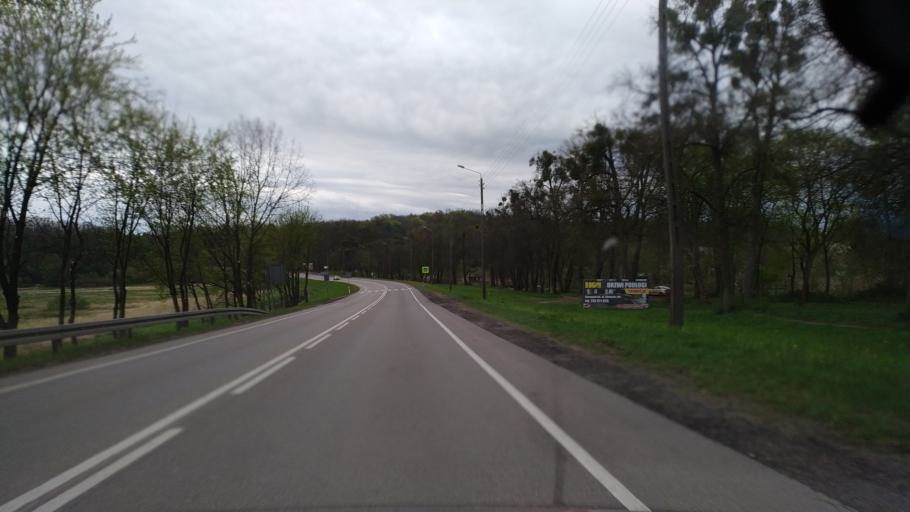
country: PL
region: Pomeranian Voivodeship
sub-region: Powiat starogardzki
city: Starogard Gdanski
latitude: 53.9717
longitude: 18.5493
